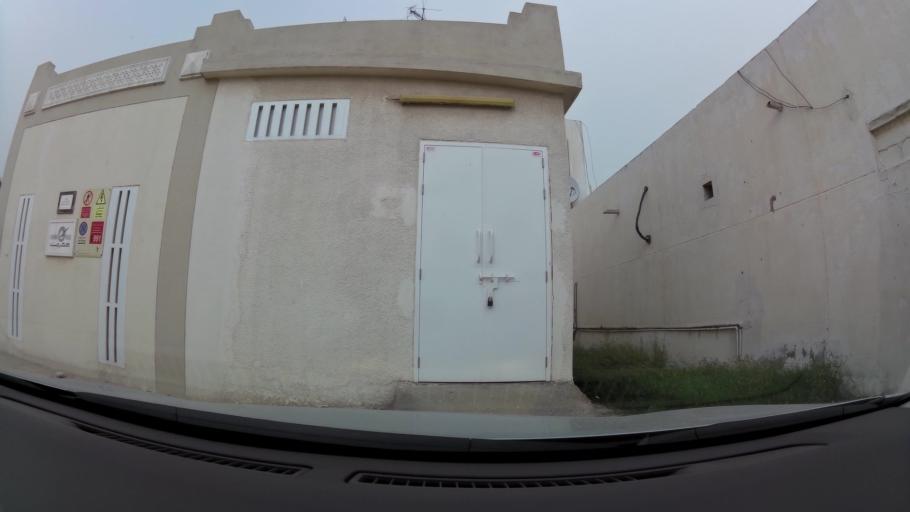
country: QA
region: Baladiyat ad Dawhah
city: Doha
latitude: 25.2580
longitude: 51.4904
